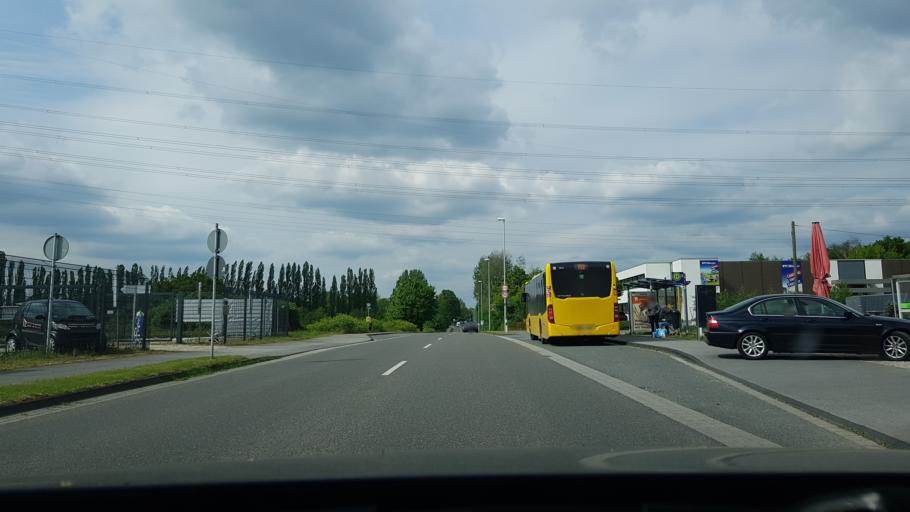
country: DE
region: North Rhine-Westphalia
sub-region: Regierungsbezirk Dusseldorf
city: Muelheim (Ruhr)
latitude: 51.3720
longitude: 6.8633
